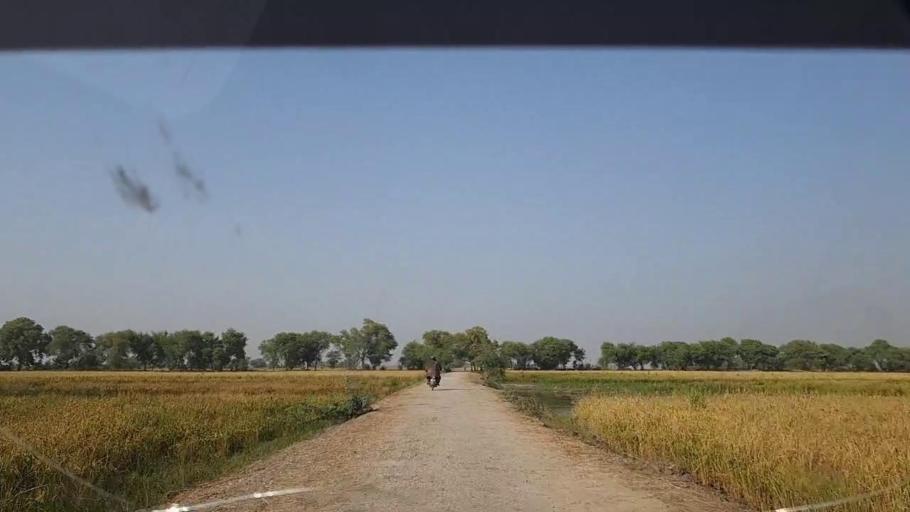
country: PK
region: Sindh
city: Shikarpur
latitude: 28.1218
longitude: 68.5831
